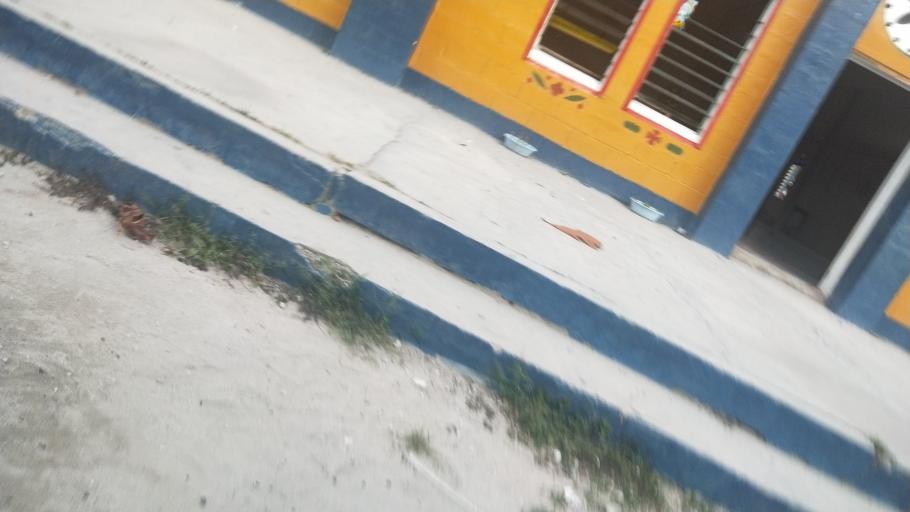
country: KI
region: Gilbert Islands
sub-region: Tarawa
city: Tarawa
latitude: 1.3292
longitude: 172.9792
